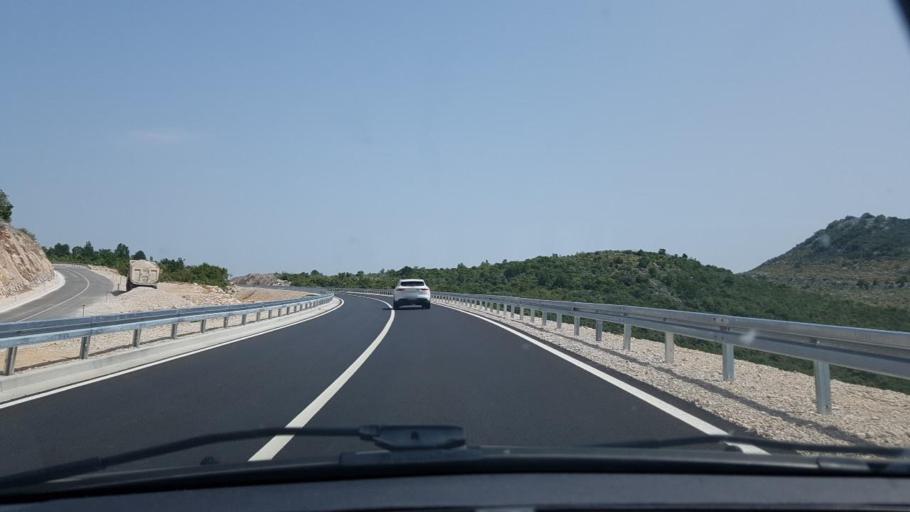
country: HR
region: Dubrovacko-Neretvanska
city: Podgora
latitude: 42.9485
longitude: 17.7604
